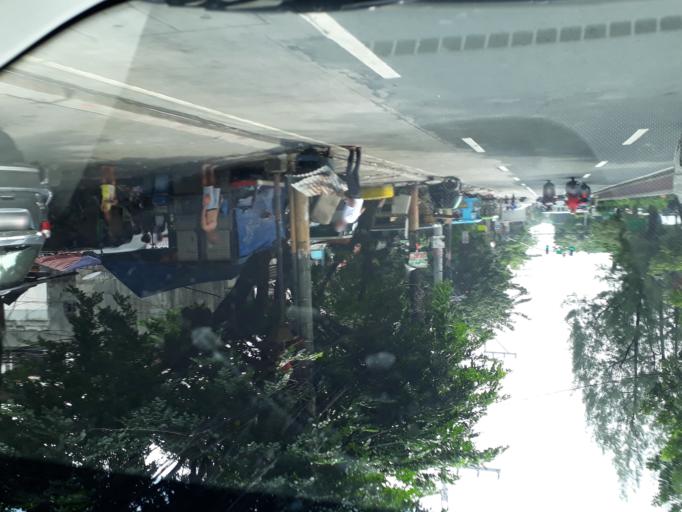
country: PH
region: Metro Manila
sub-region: City of Manila
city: Manila
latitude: 14.6145
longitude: 120.9881
